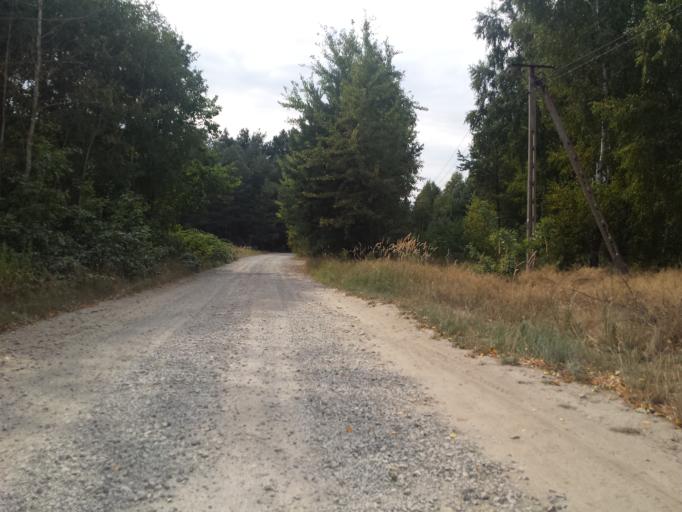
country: PL
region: Swietokrzyskie
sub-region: Powiat kielecki
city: Rakow
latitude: 50.6673
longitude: 21.1446
